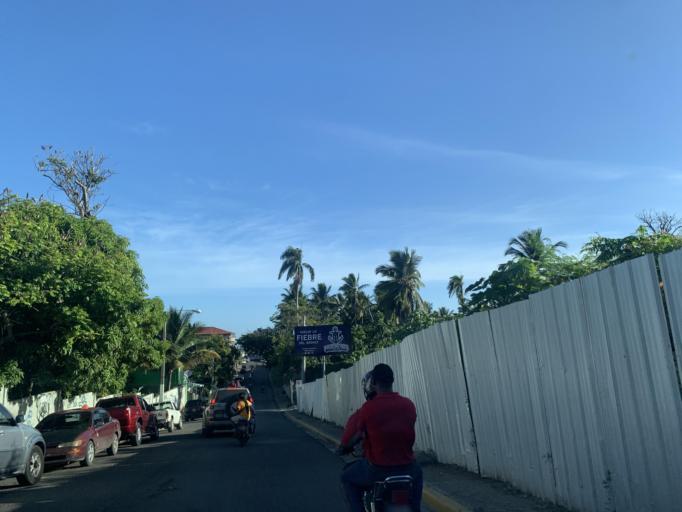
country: DO
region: Puerto Plata
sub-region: Puerto Plata
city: Puerto Plata
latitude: 19.7911
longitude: -70.6909
